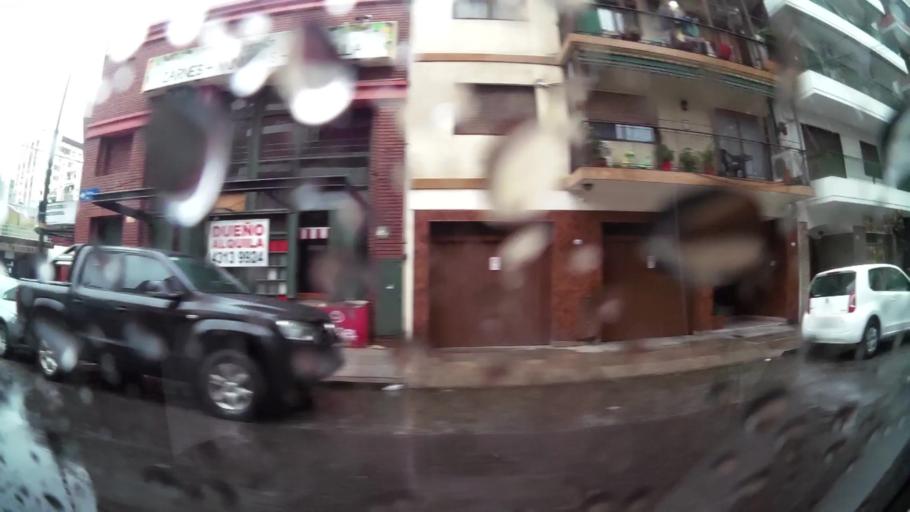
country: AR
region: Buenos Aires F.D.
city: Buenos Aires
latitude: -34.6332
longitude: -58.3724
